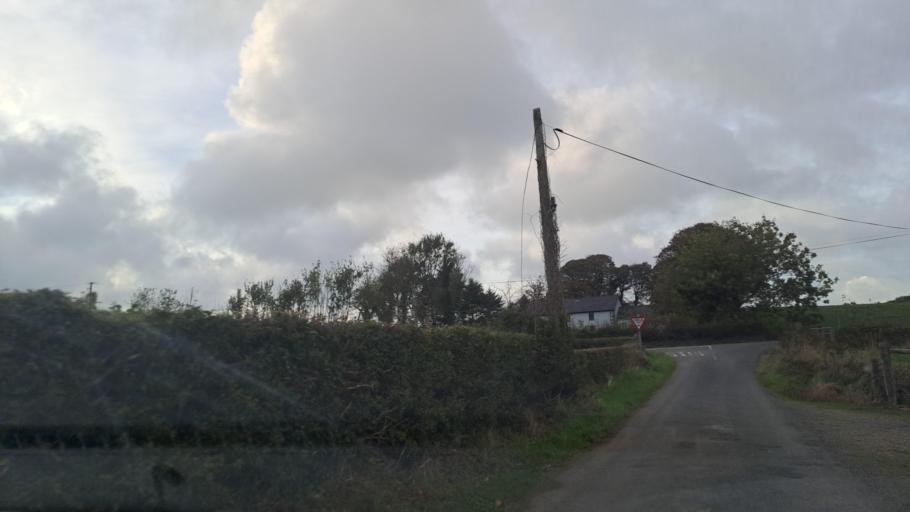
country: IE
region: Ulster
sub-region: County Monaghan
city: Carrickmacross
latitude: 54.0282
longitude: -6.7754
